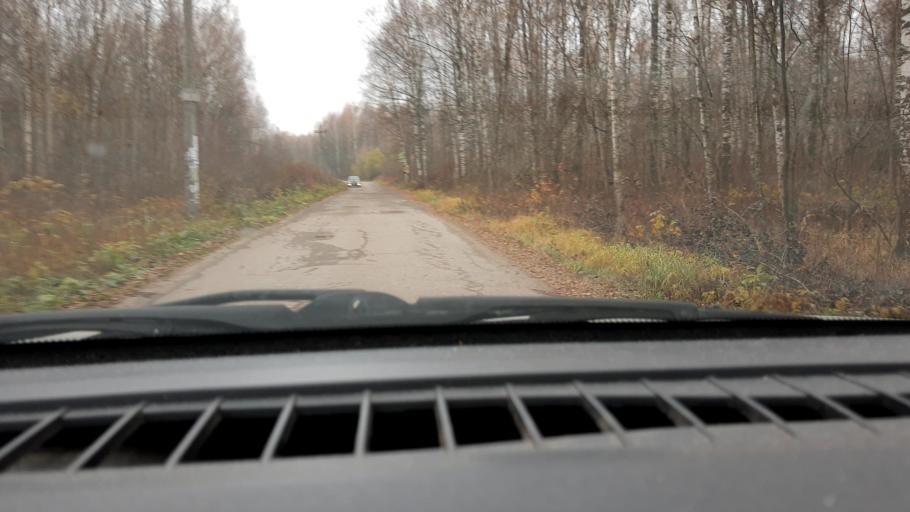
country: RU
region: Nizjnij Novgorod
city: Gorbatovka
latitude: 56.3075
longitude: 43.7250
